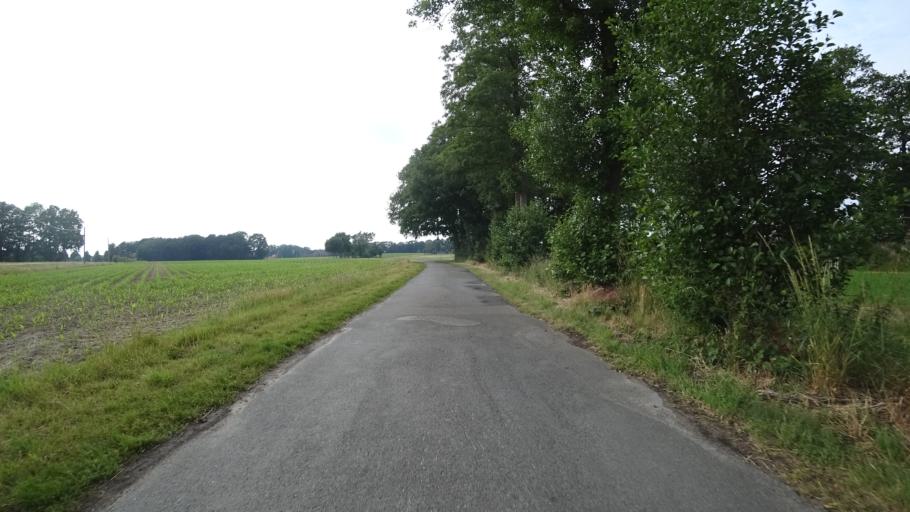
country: DE
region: North Rhine-Westphalia
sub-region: Regierungsbezirk Detmold
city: Guetersloh
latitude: 51.9487
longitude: 8.3740
